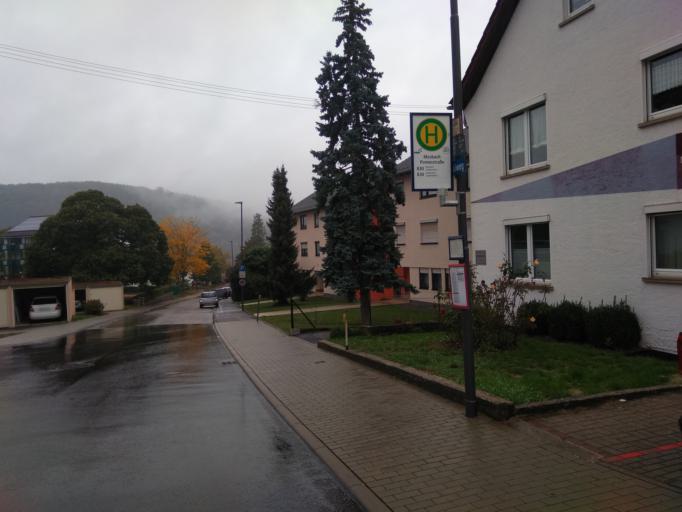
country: DE
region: Baden-Wuerttemberg
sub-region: Karlsruhe Region
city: Mosbach
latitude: 49.3534
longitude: 9.1531
